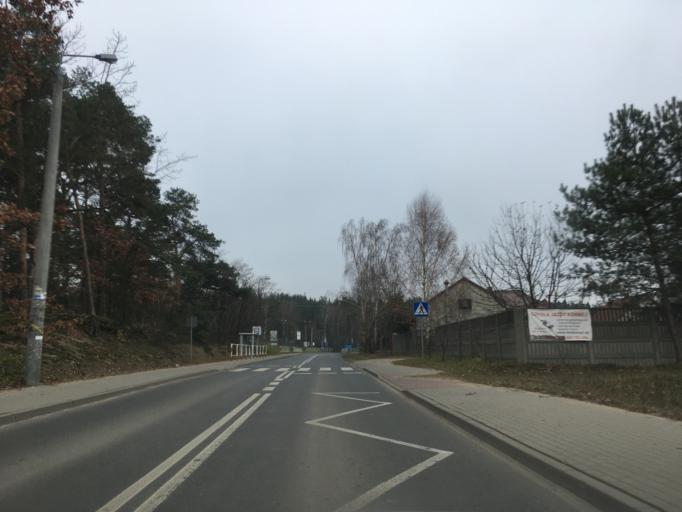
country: PL
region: Masovian Voivodeship
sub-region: Powiat piaseczynski
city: Lesznowola
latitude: 52.0683
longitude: 20.9341
